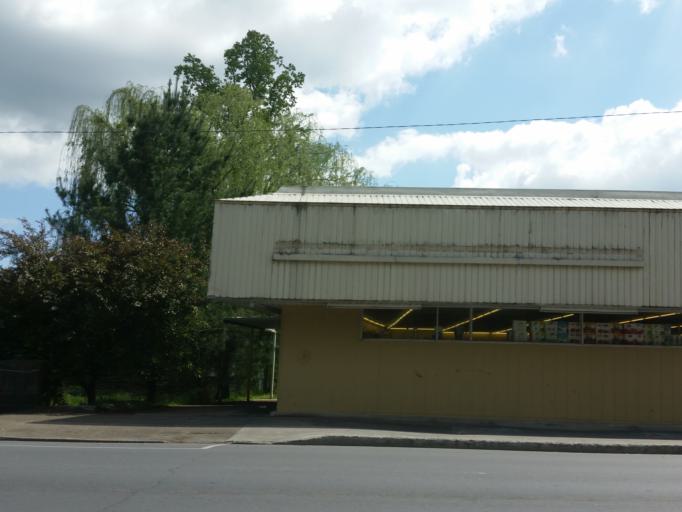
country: US
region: Kentucky
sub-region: Bell County
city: Middlesboro
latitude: 36.6070
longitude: -83.7185
